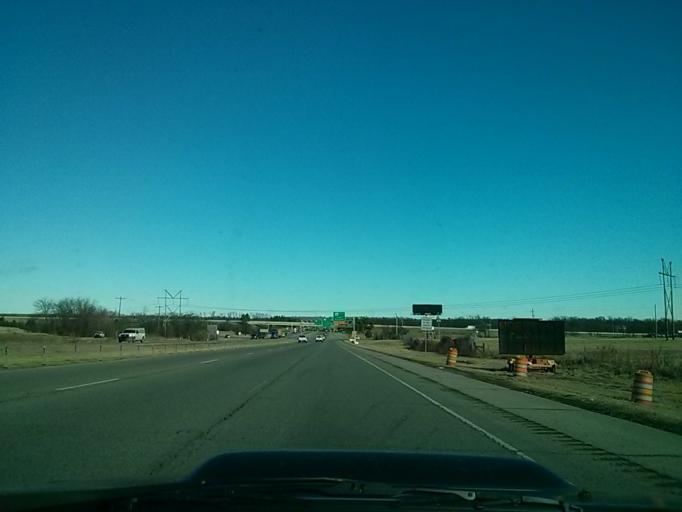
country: US
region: Oklahoma
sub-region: Tulsa County
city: Jenks
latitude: 36.0038
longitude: -96.0115
